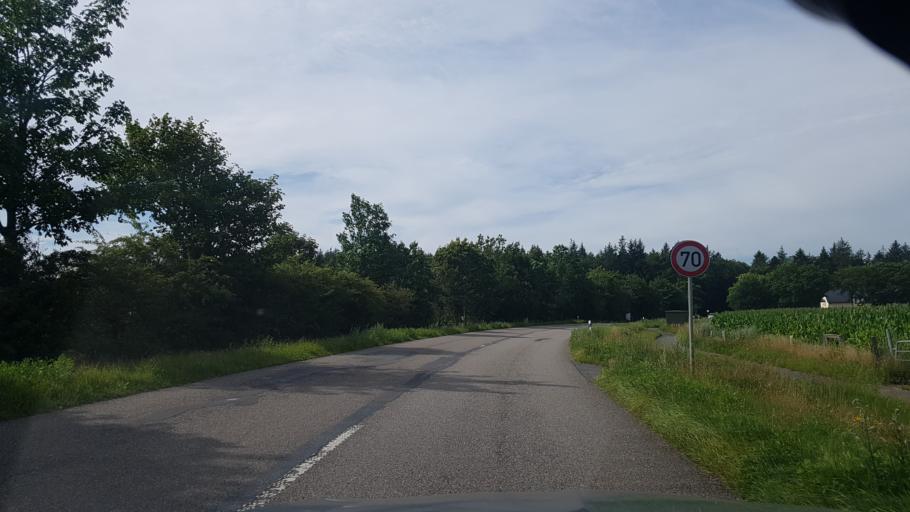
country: DE
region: Schleswig-Holstein
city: Bramstedtlund
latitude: 54.8613
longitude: 9.0470
